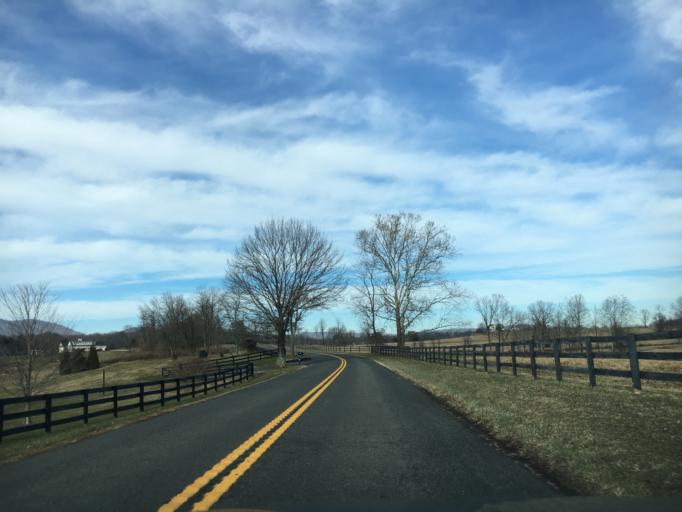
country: US
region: Virginia
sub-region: Fauquier County
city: Marshall
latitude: 38.8120
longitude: -77.9983
